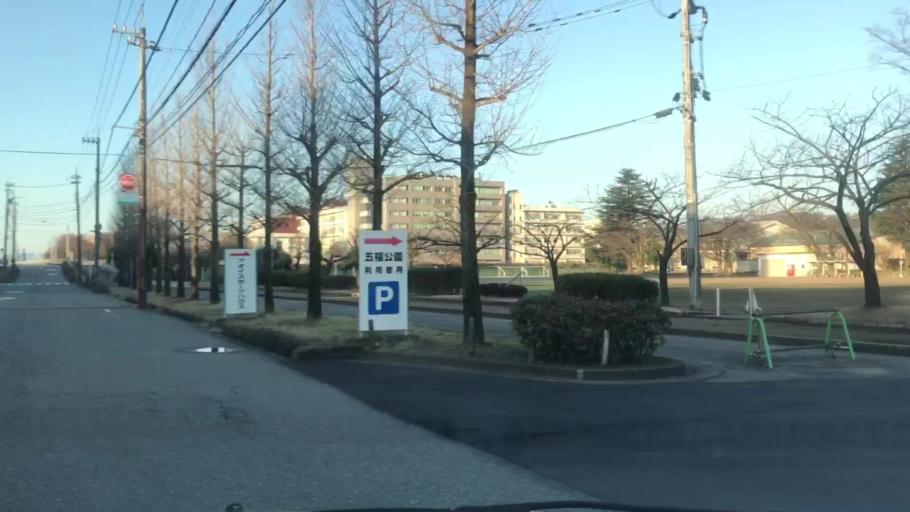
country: JP
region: Toyama
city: Toyama-shi
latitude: 36.6953
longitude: 137.1902
